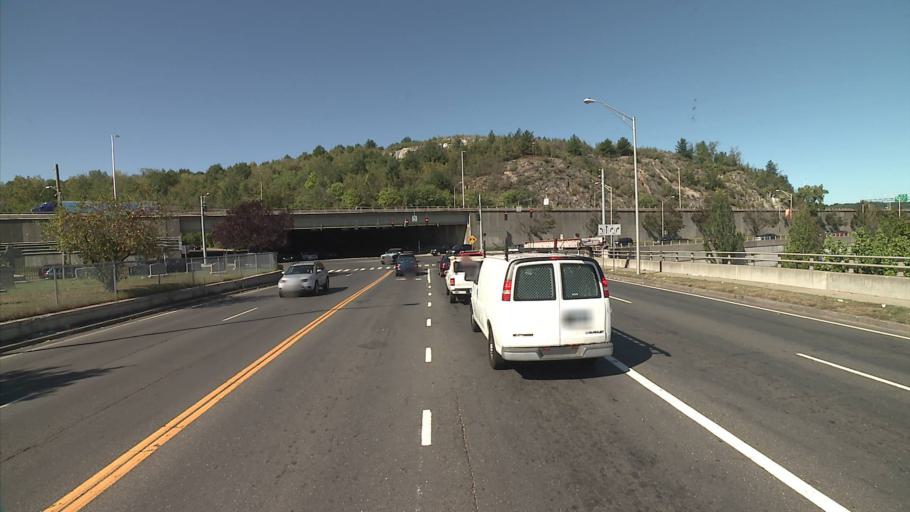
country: US
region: Connecticut
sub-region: New Haven County
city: Waterbury
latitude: 41.5463
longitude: -73.0257
